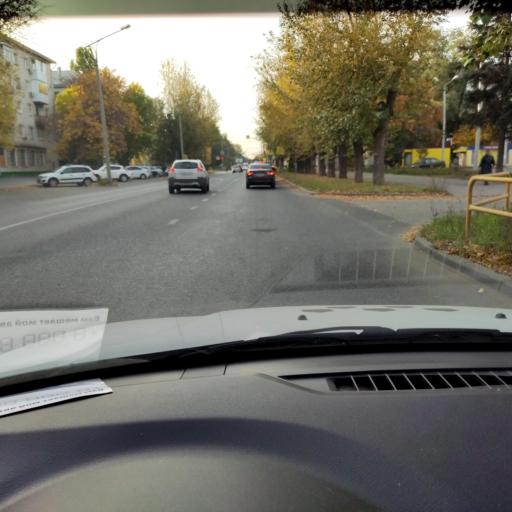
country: RU
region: Samara
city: Tol'yatti
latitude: 53.5320
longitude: 49.4116
